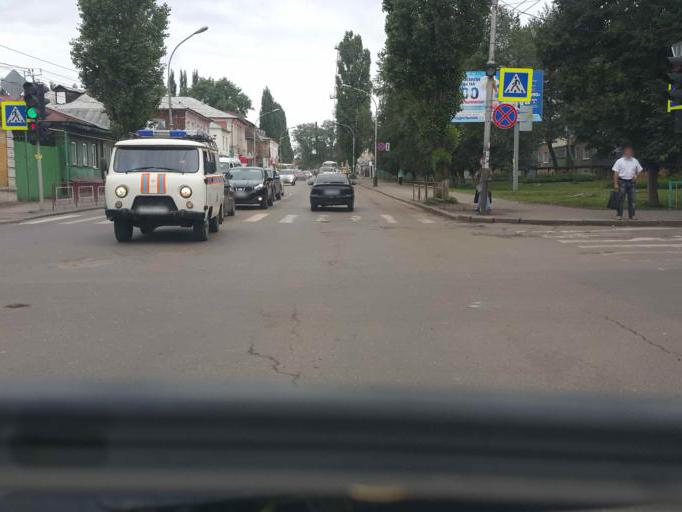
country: RU
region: Tambov
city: Michurinsk
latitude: 52.8928
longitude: 40.5017
